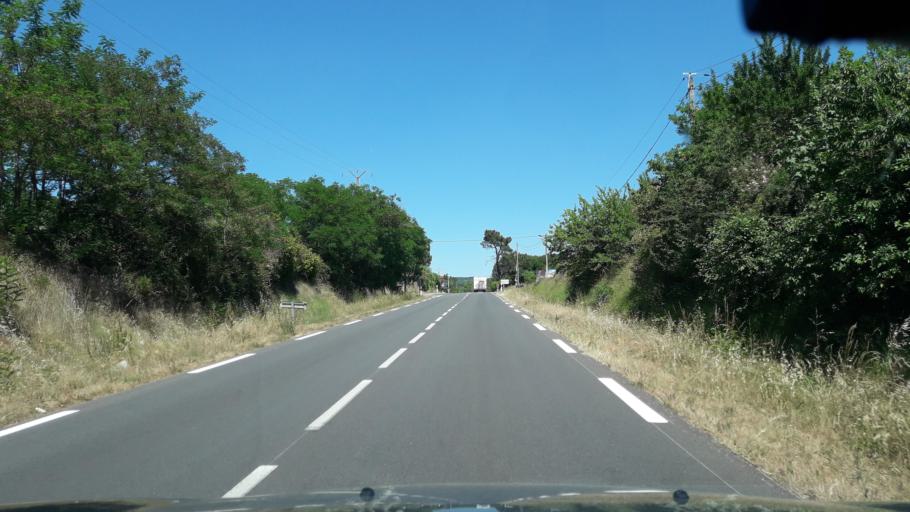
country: FR
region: Rhone-Alpes
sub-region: Departement de l'Ardeche
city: Ruoms
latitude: 44.4283
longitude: 4.3307
